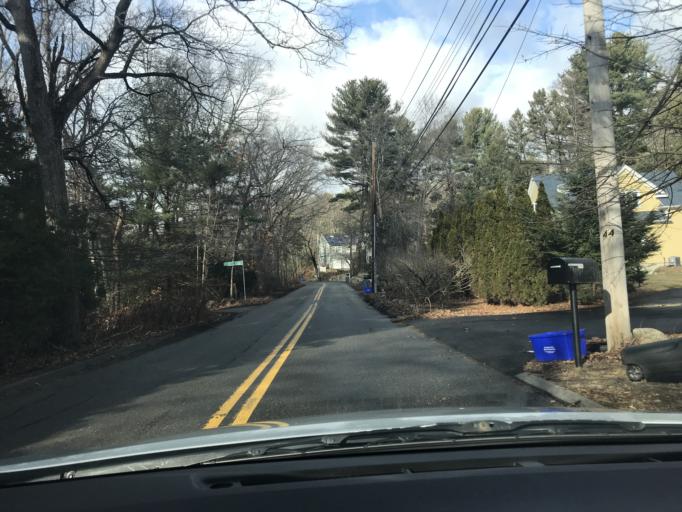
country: US
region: Massachusetts
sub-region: Middlesex County
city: Lexington
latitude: 42.4707
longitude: -71.2184
